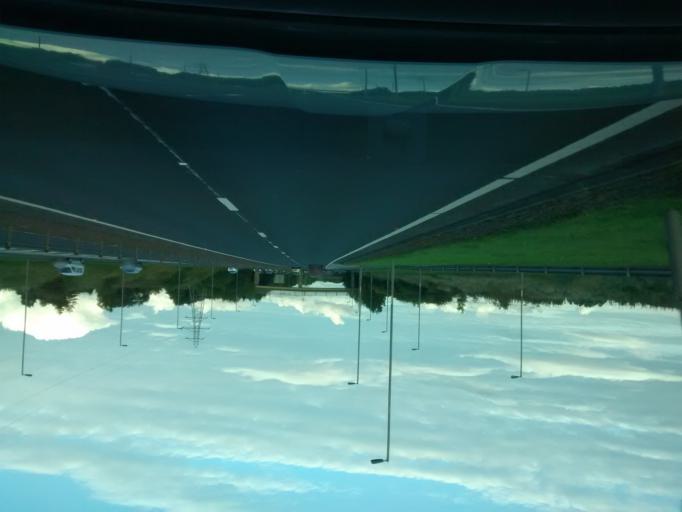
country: GB
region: Scotland
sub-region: Renfrewshire
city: Johnstone
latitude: 55.8403
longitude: -4.5161
